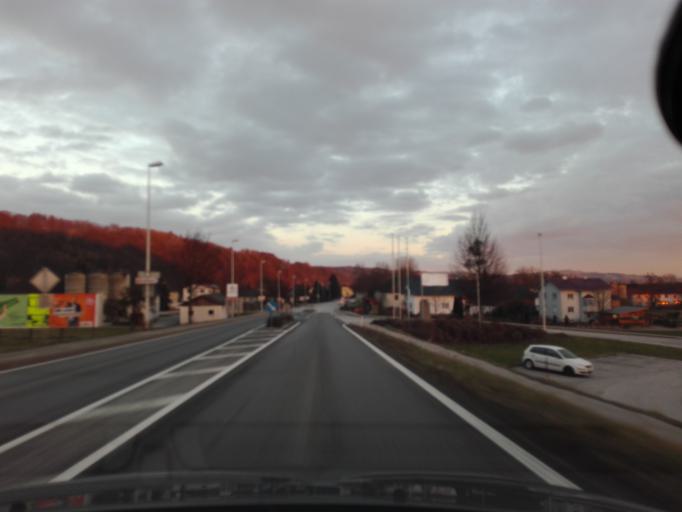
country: AT
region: Upper Austria
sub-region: Politischer Bezirk Perg
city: Bad Kreuzen
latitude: 48.2130
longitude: 14.7564
